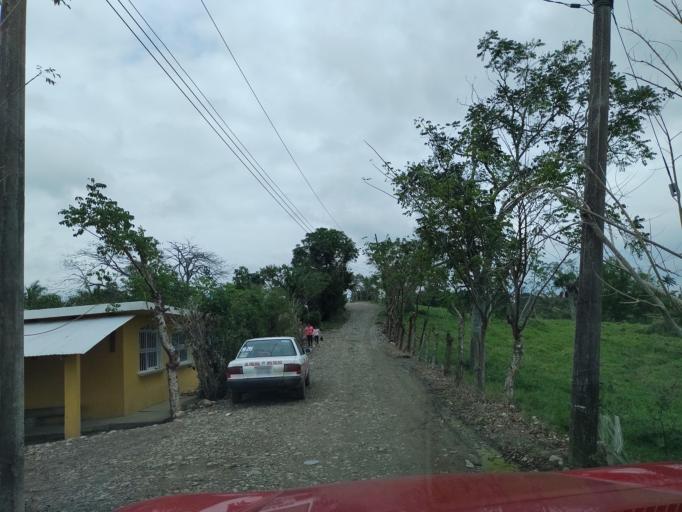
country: MX
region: Veracruz
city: Coatzintla
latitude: 20.4577
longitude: -97.4146
